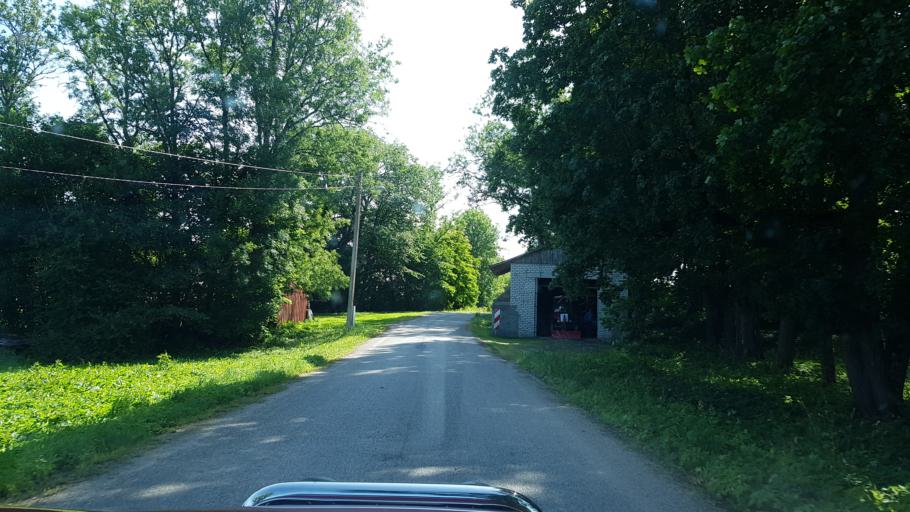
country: EE
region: Jaervamaa
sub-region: Jaerva-Jaani vald
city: Jarva-Jaani
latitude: 59.0896
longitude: 25.7272
